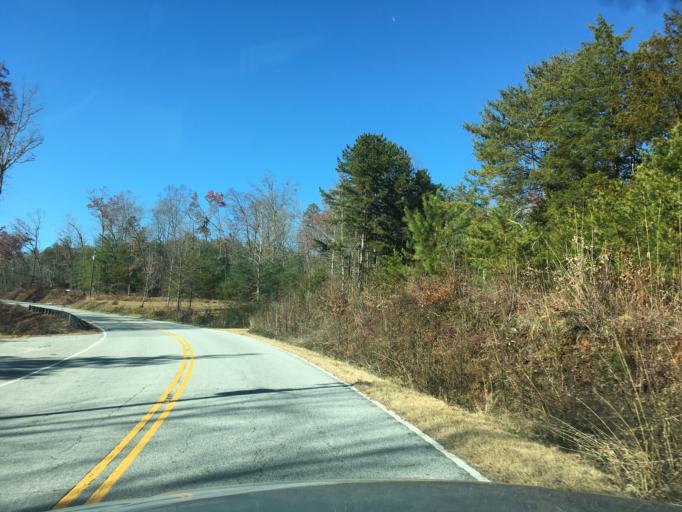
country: US
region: South Carolina
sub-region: Oconee County
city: Walhalla
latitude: 34.9326
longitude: -82.9899
